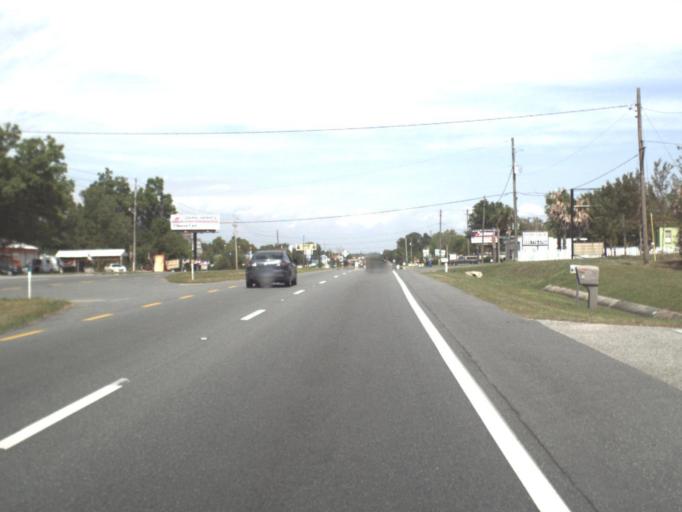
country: US
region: Florida
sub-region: Santa Rosa County
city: Pace
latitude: 30.5950
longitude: -87.1712
